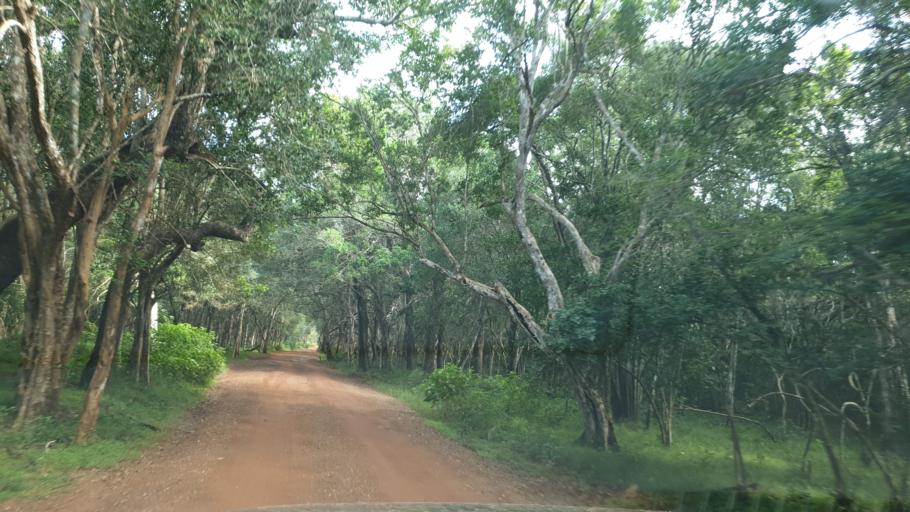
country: LK
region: North Central
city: Anuradhapura
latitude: 8.3798
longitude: 80.0667
